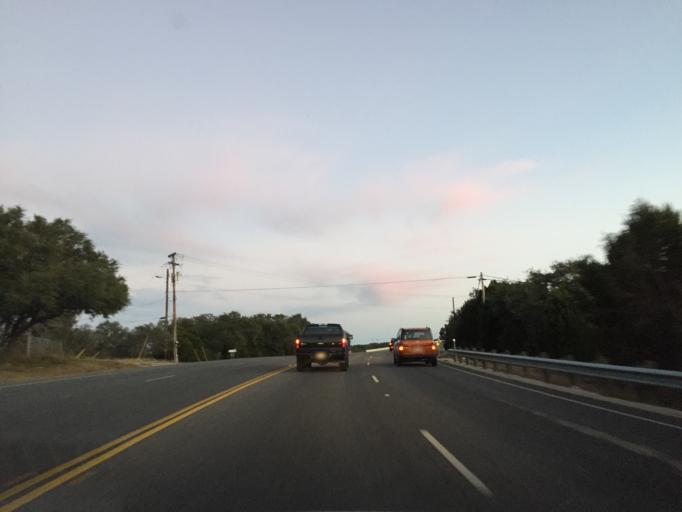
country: US
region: Texas
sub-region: Travis County
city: Jonestown
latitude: 30.5174
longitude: -97.8897
